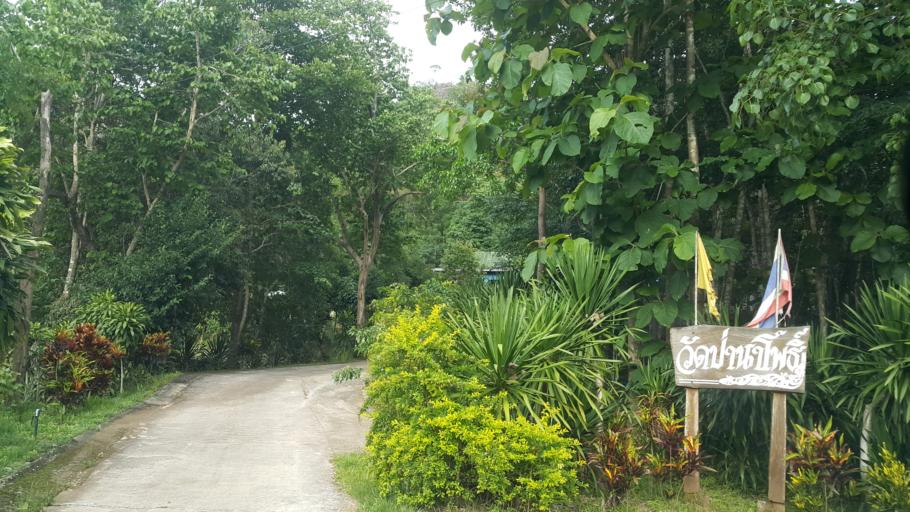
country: TH
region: Loei
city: Na Haeo
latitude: 17.4988
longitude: 101.0829
